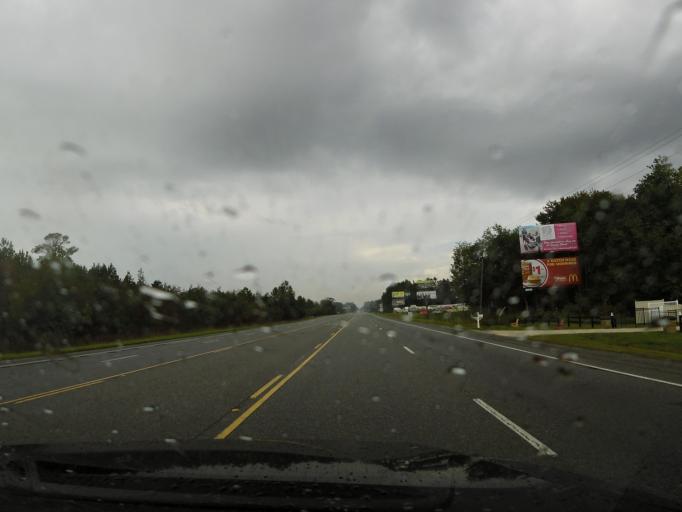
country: US
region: Georgia
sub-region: Wayne County
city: Jesup
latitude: 31.5837
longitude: -81.8570
